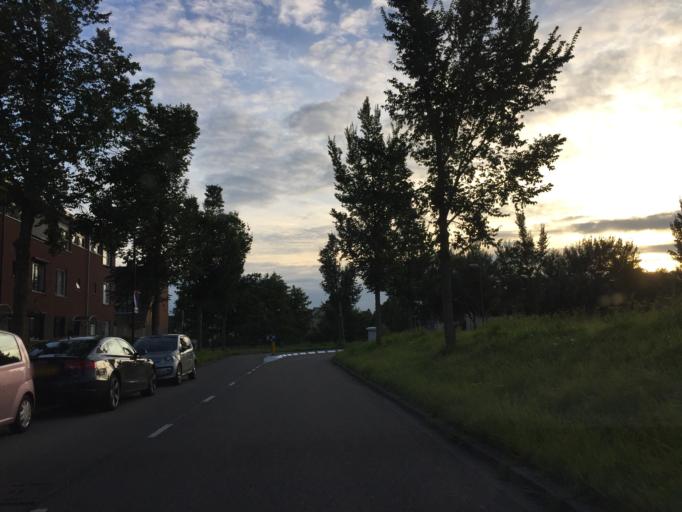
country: NL
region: South Holland
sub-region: Gemeente Rijnwoude
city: Benthuizen
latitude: 52.0774
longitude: 4.5270
